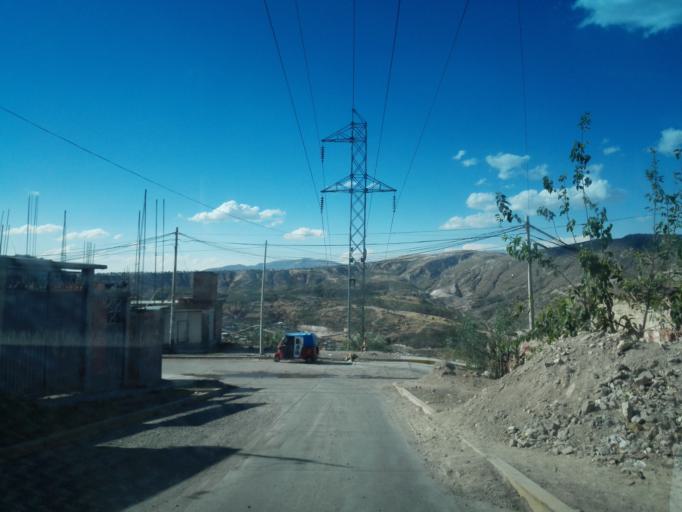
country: PE
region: Ayacucho
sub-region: Provincia de Huamanga
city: Ayacucho
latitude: -13.1459
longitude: -74.2155
